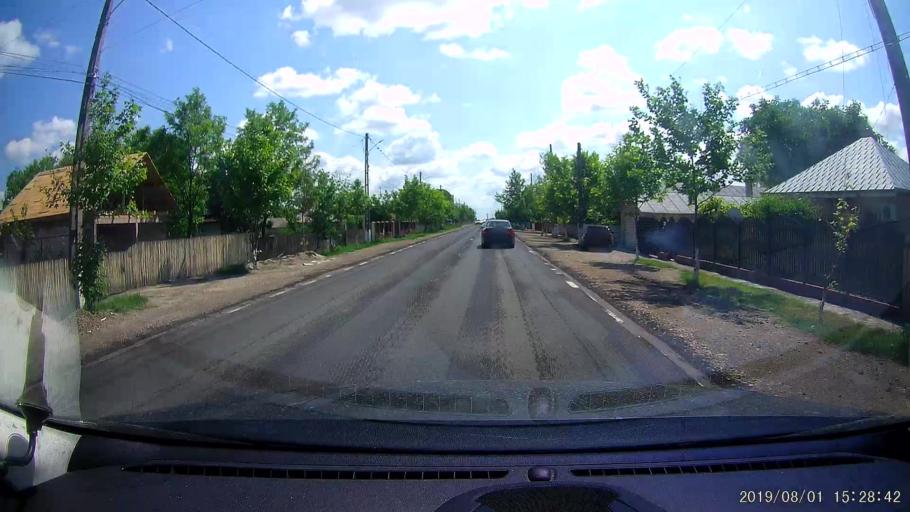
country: RO
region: Braila
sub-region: Comuna Viziru
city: Viziru
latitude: 44.9911
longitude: 27.7066
